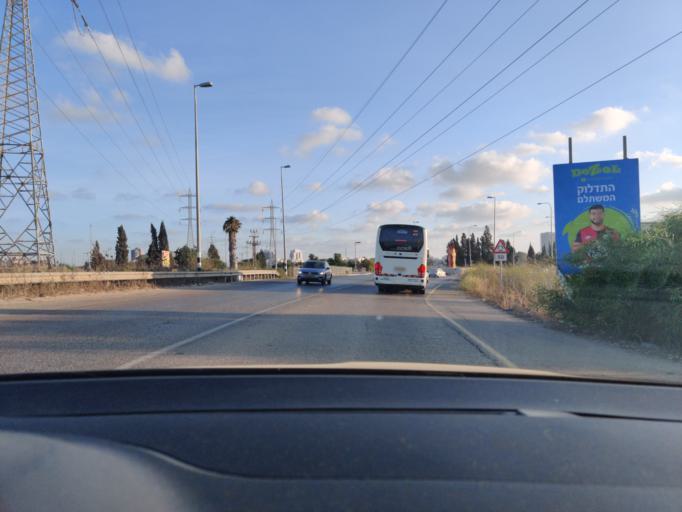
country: IL
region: Haifa
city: Hadera
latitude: 32.4442
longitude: 34.9390
